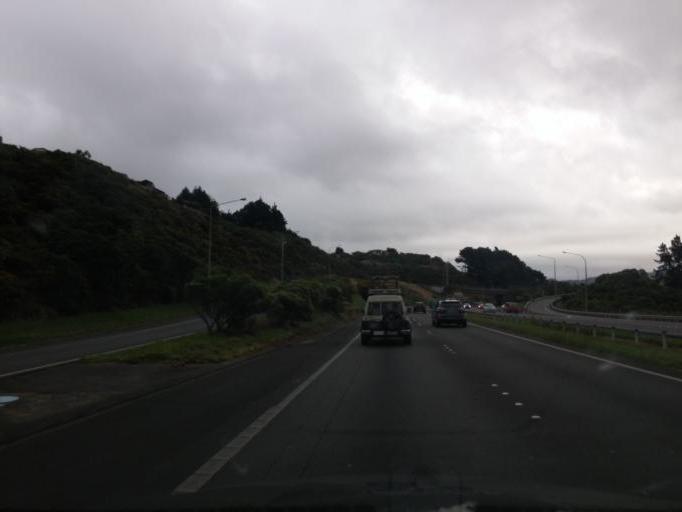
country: NZ
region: Wellington
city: Petone
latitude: -41.2024
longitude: 174.8228
